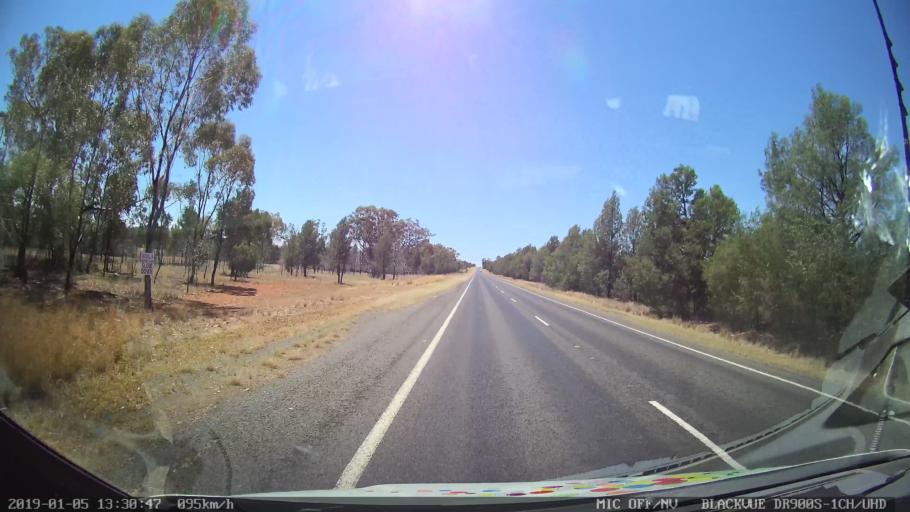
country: AU
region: New South Wales
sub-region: Gunnedah
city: Gunnedah
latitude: -31.0160
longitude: 150.0753
